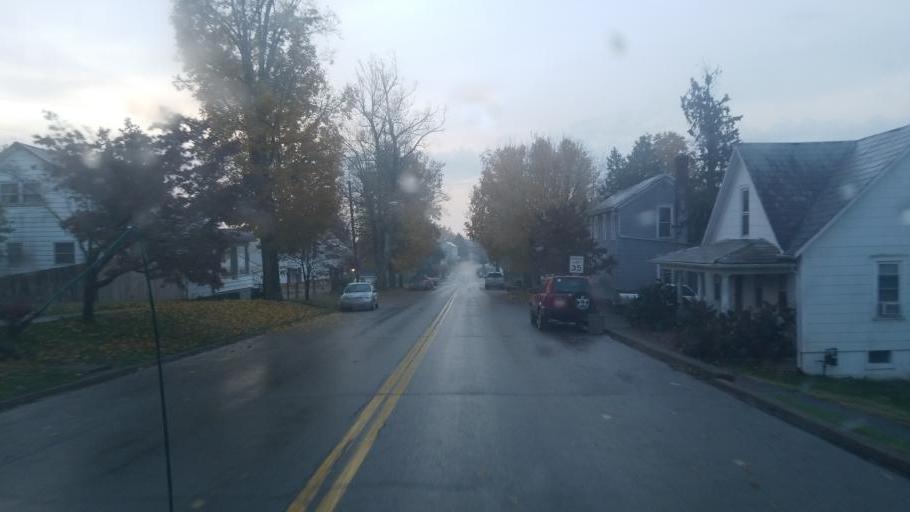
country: US
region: Ohio
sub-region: Morgan County
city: McConnelsville
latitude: 39.4920
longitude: -81.8649
